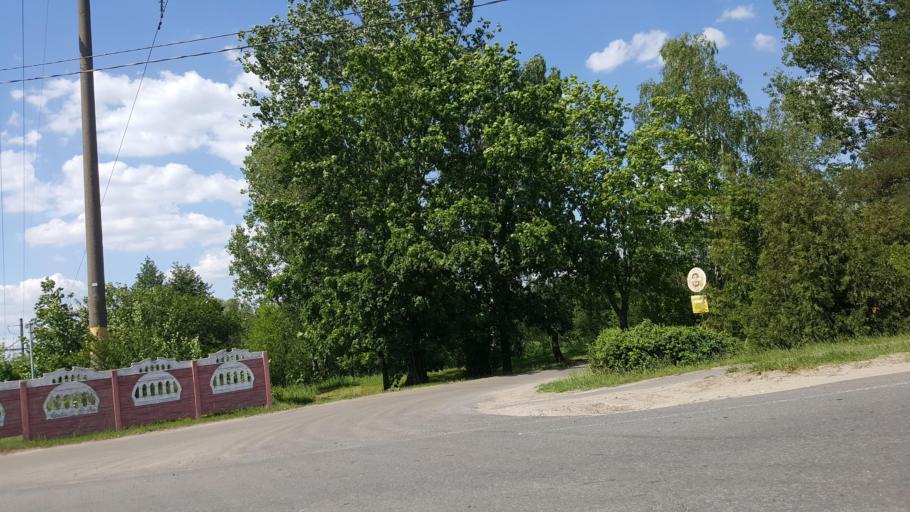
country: BY
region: Brest
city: Horad Kobryn
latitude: 52.2137
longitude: 24.3774
